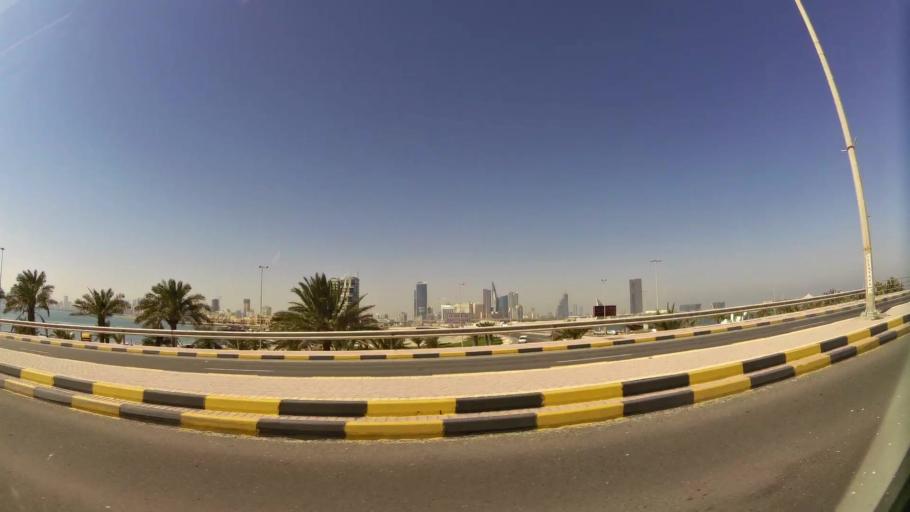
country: BH
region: Muharraq
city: Al Muharraq
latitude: 26.2496
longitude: 50.6060
